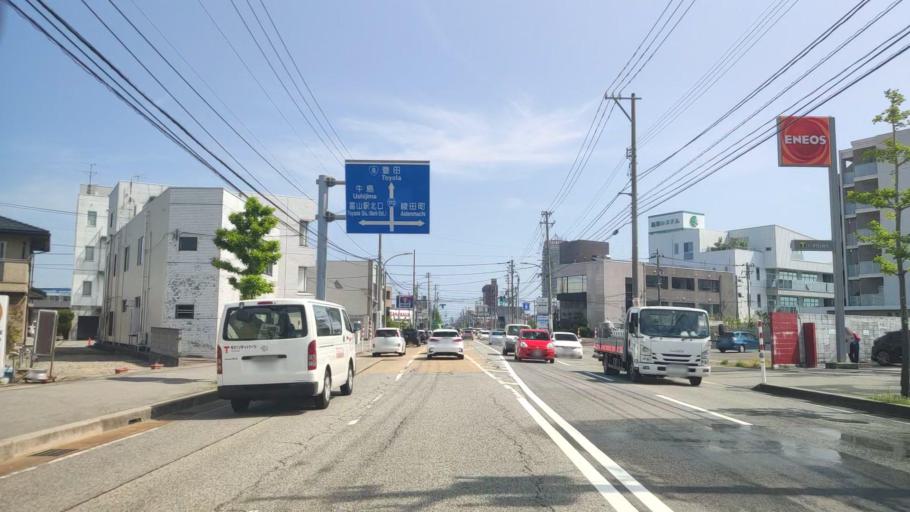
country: JP
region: Toyama
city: Toyama-shi
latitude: 36.7019
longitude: 137.2271
